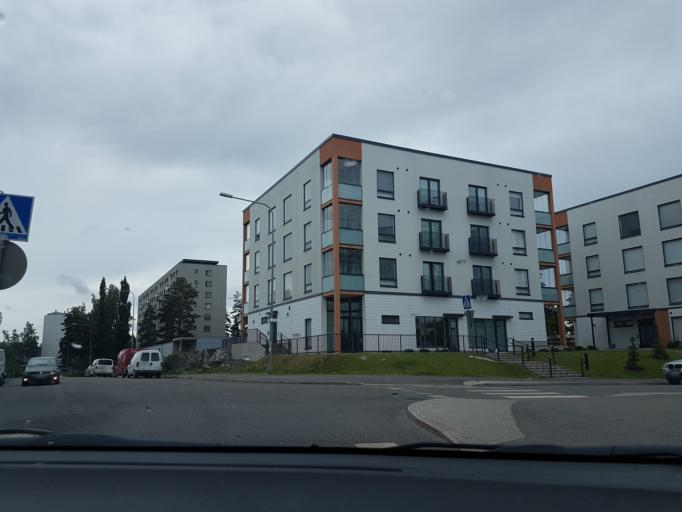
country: FI
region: Uusimaa
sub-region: Helsinki
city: Vantaa
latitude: 60.2392
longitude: 25.0861
